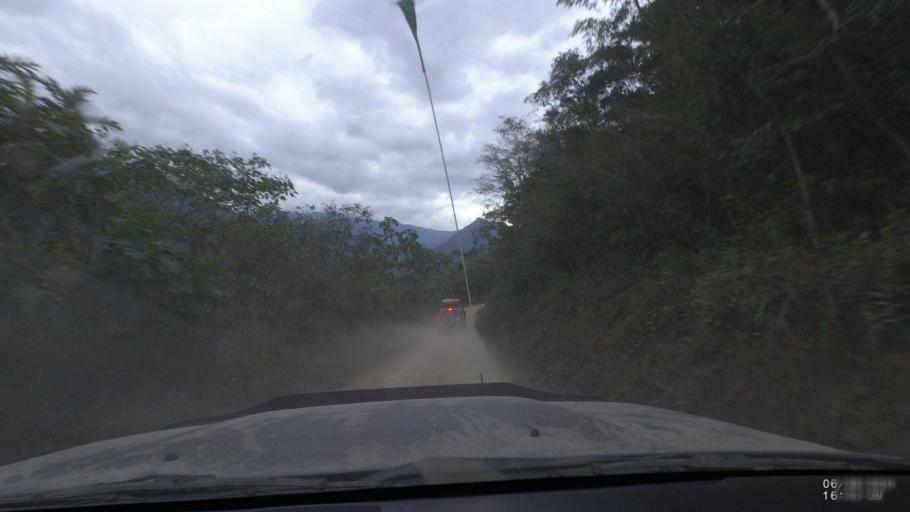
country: BO
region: La Paz
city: Quime
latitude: -16.4930
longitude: -66.7780
